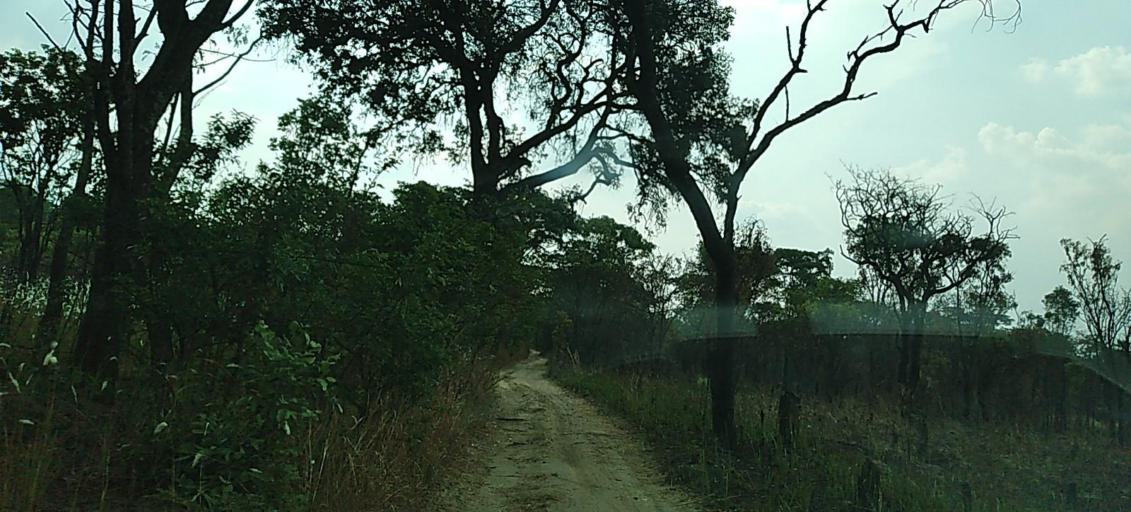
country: ZM
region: North-Western
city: Solwezi
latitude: -12.0782
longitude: 26.2445
